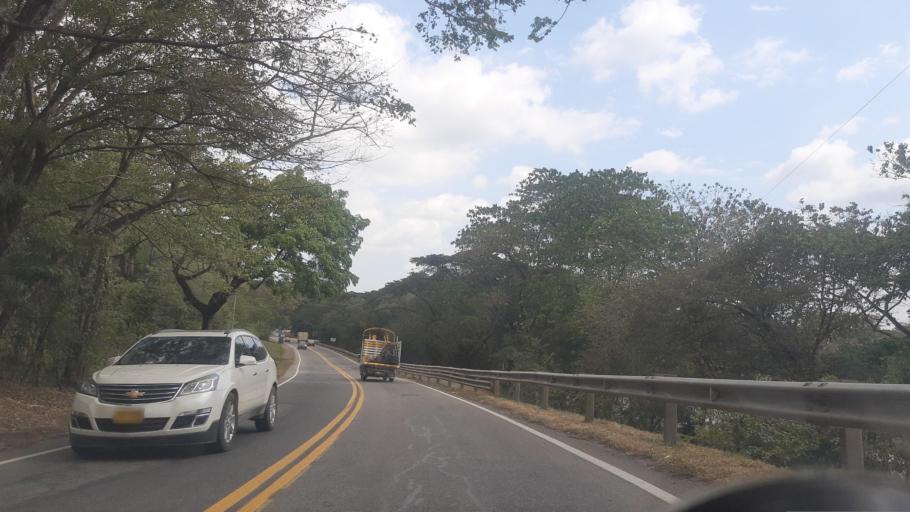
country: CO
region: Casanare
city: Tauramena
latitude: 5.0120
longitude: -72.6791
